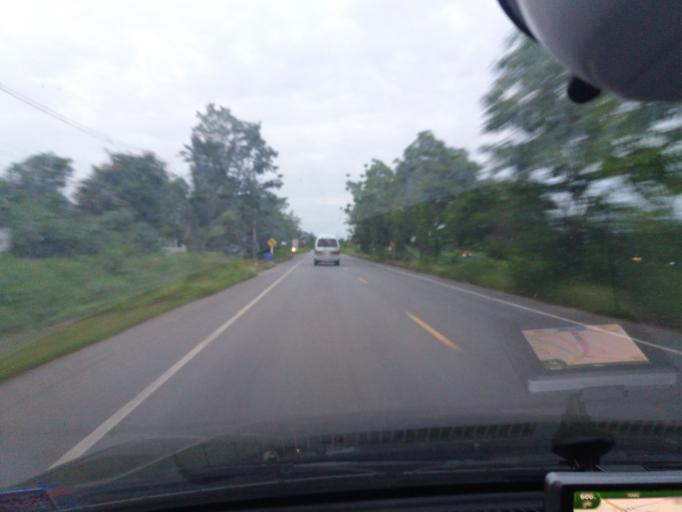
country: TH
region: Suphan Buri
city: Ban Sam Chuk
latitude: 14.7417
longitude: 100.0924
